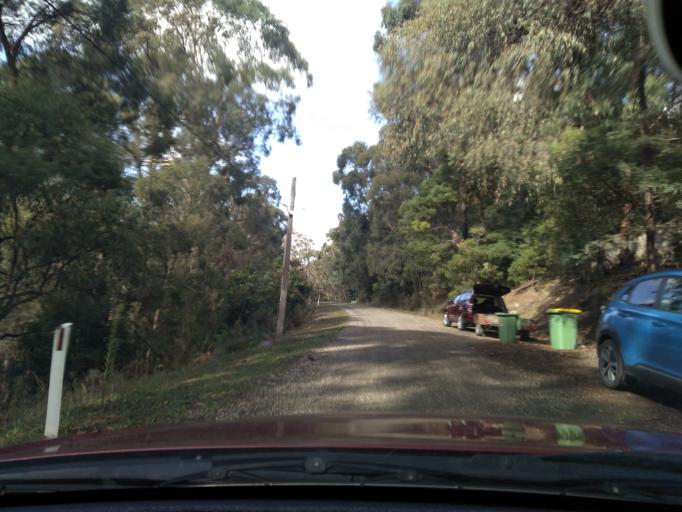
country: AU
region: Victoria
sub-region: Cardinia
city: Cockatoo
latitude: -37.9511
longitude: 145.4683
